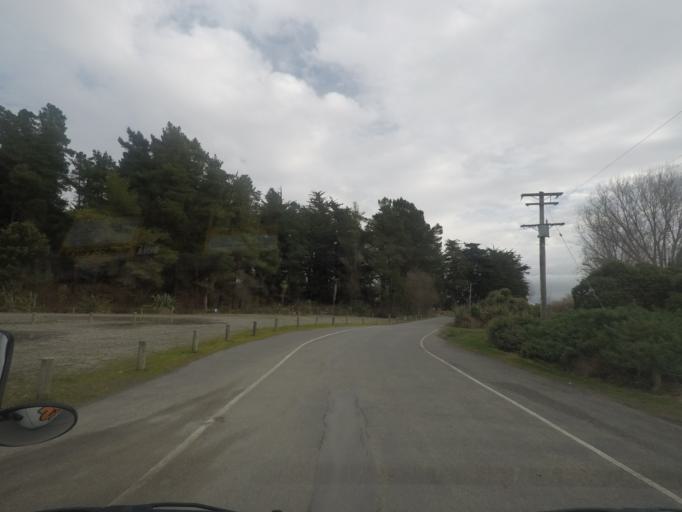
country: NZ
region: Canterbury
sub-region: Waimakariri District
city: Woodend
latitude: -43.2880
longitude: 172.7202
